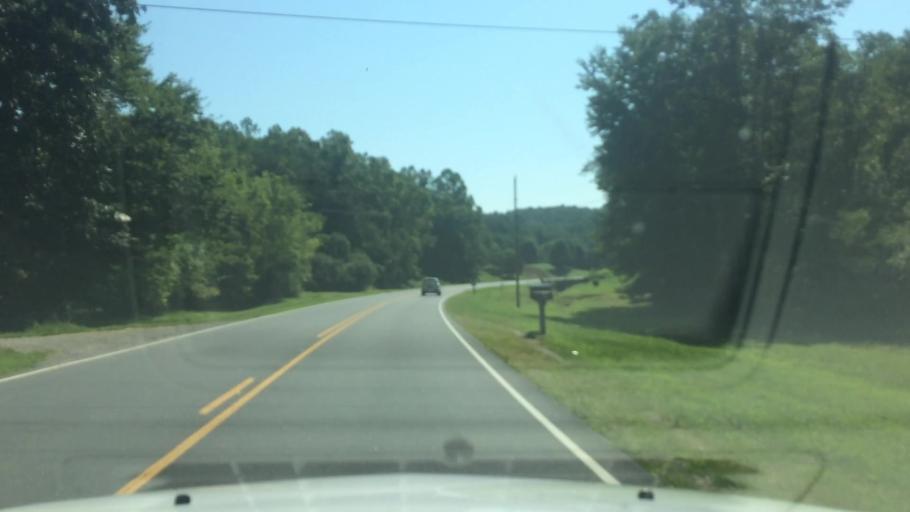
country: US
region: North Carolina
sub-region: Caldwell County
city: Lenoir
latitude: 35.9180
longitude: -81.4616
